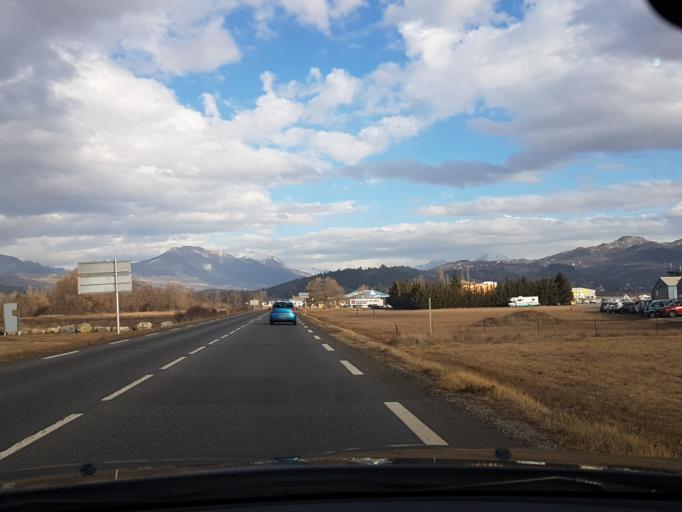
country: FR
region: Provence-Alpes-Cote d'Azur
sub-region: Departement des Hautes-Alpes
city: Tallard
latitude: 44.4524
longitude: 6.0329
